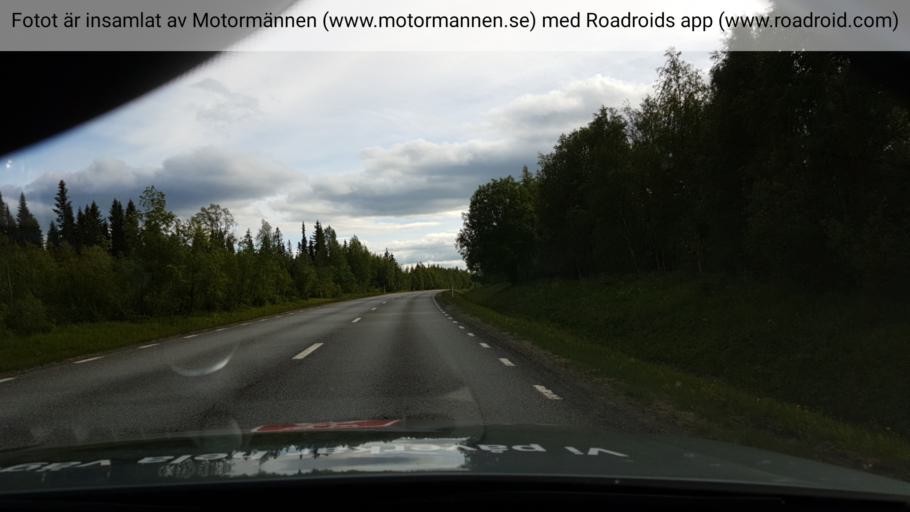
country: SE
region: Jaemtland
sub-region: OEstersunds Kommun
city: Lit
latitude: 63.4618
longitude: 15.1823
